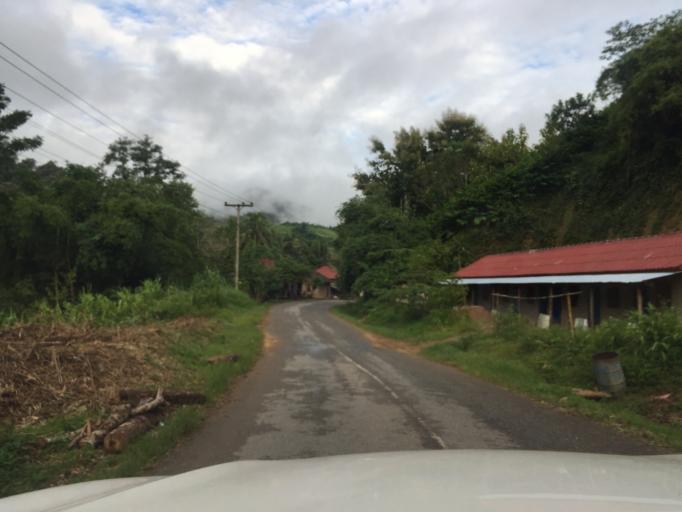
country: LA
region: Phongsali
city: Khoa
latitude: 21.1013
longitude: 102.2621
